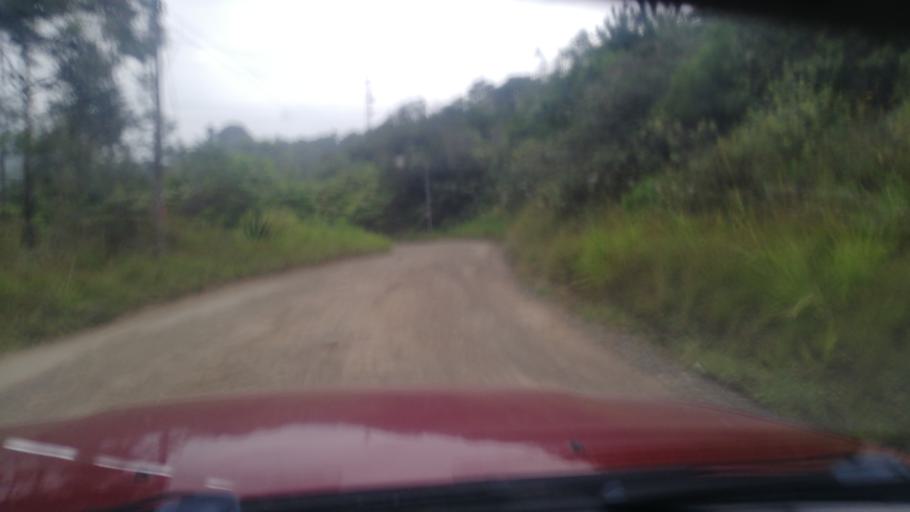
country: CO
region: Valle del Cauca
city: Cali
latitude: 3.4935
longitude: -76.5481
